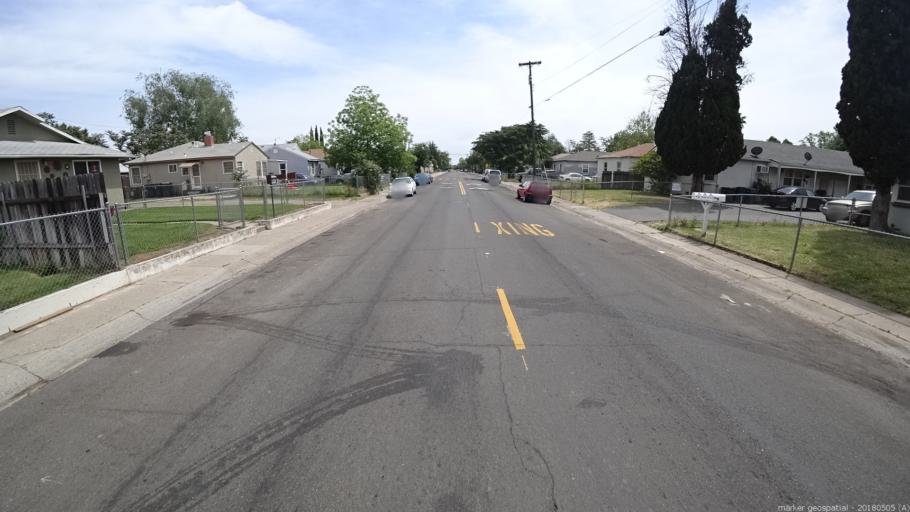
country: US
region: California
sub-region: Sacramento County
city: Arden-Arcade
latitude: 38.6328
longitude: -121.4263
